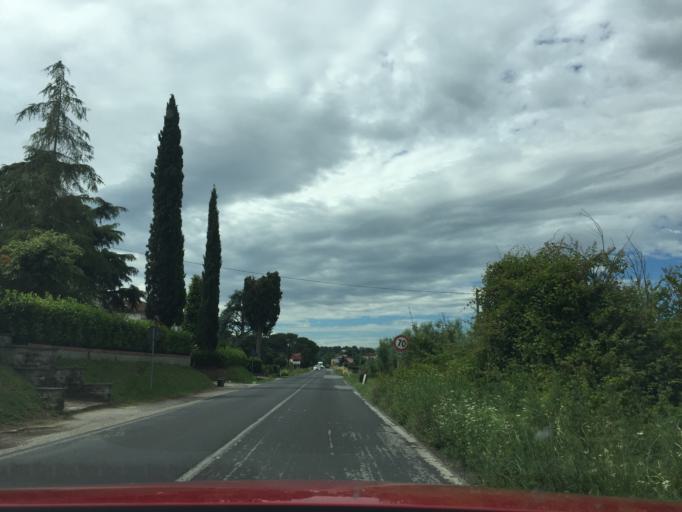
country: IT
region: Tuscany
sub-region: Province of Florence
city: Fucecchio
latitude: 43.7498
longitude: 10.8205
